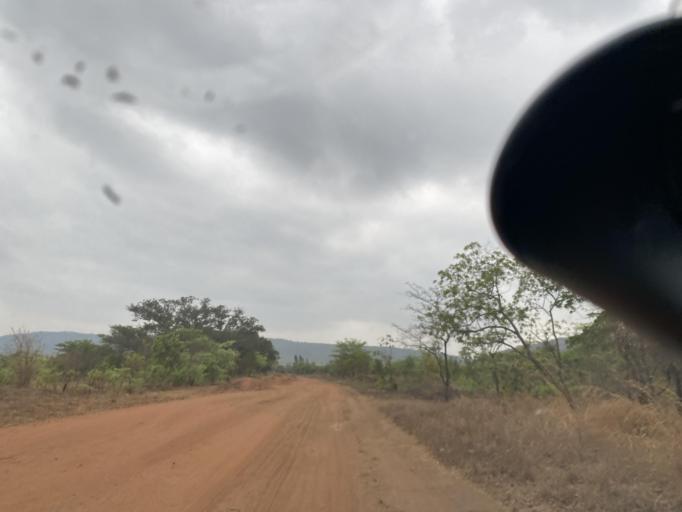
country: ZM
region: Lusaka
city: Chongwe
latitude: -15.1938
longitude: 28.7656
